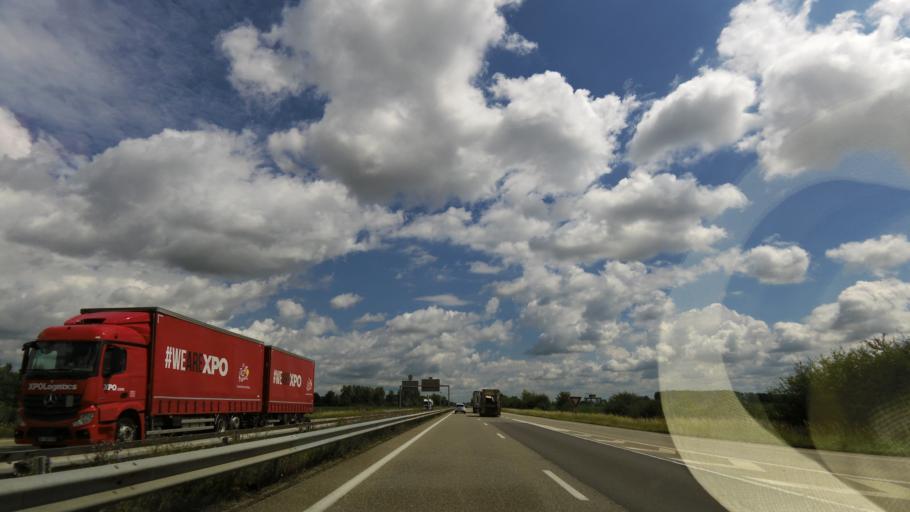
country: FR
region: Alsace
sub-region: Departement du Bas-Rhin
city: Gambsheim
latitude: 48.7079
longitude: 7.8575
